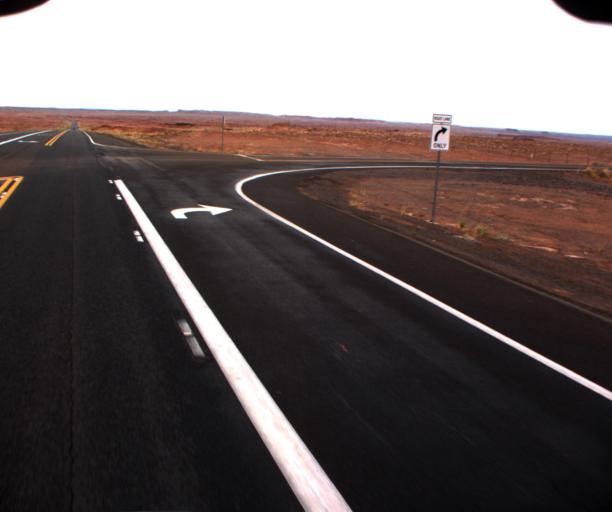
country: US
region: Arizona
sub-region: Coconino County
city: Tuba City
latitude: 36.1005
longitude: -111.3163
